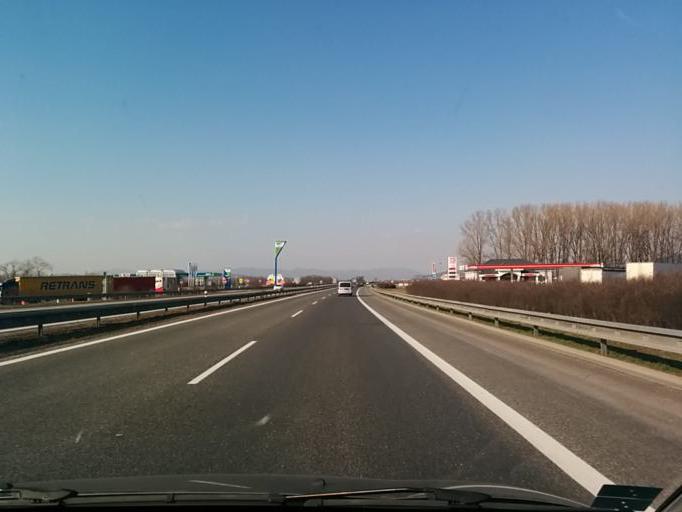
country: SK
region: Trenciansky
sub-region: Okres Nove Mesto nad Vahom
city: Nove Mesto nad Vahom
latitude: 48.7063
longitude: 17.8720
